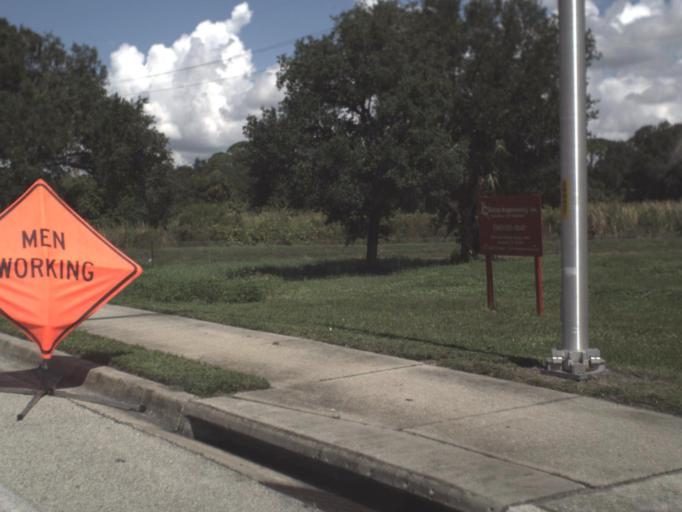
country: US
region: Florida
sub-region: Sarasota County
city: South Venice
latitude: 27.0566
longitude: -82.4123
